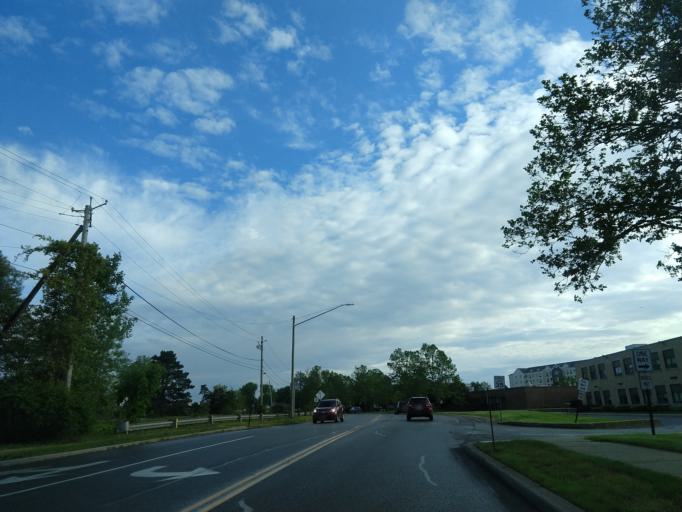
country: US
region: New York
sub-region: Erie County
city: West Seneca
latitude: 42.8354
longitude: -78.7886
